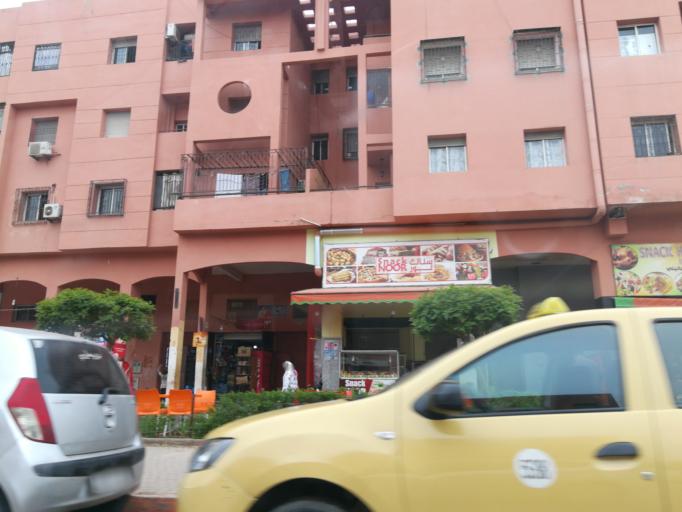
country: MA
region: Marrakech-Tensift-Al Haouz
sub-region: Marrakech
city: Marrakesh
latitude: 31.5767
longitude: -8.0603
